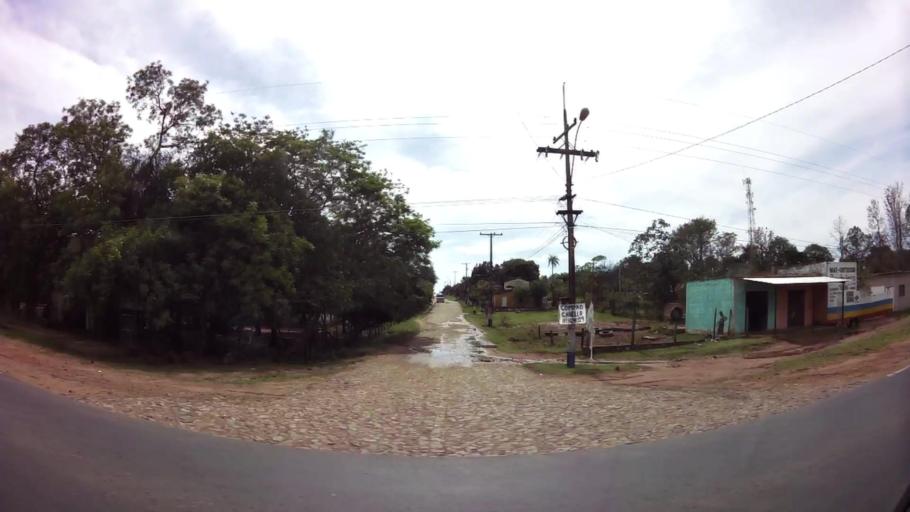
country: PY
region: Presidente Hayes
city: Villa Hayes
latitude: -25.1132
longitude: -57.4890
